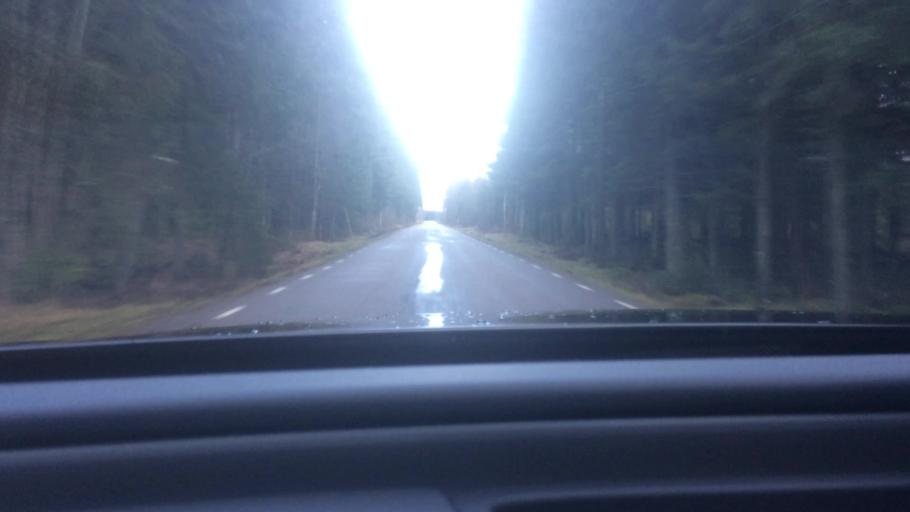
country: SE
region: Vaestra Goetaland
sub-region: Falkopings Kommun
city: Falkoeping
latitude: 58.0214
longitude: 13.5168
